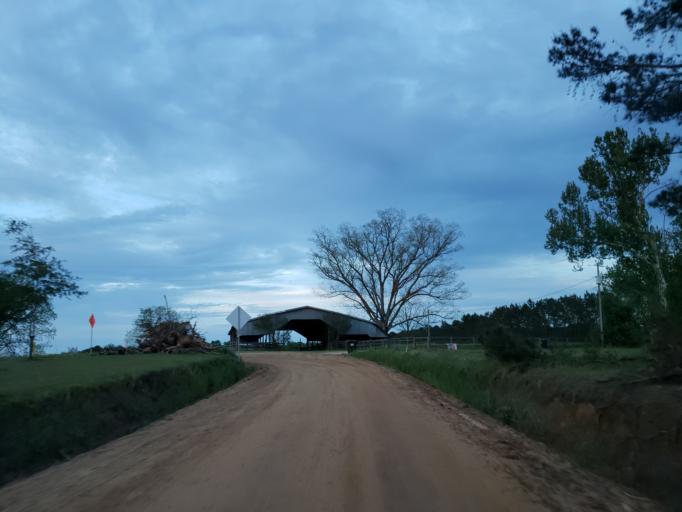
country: US
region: Georgia
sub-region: Lowndes County
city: Hahira
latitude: 30.9603
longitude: -83.3909
